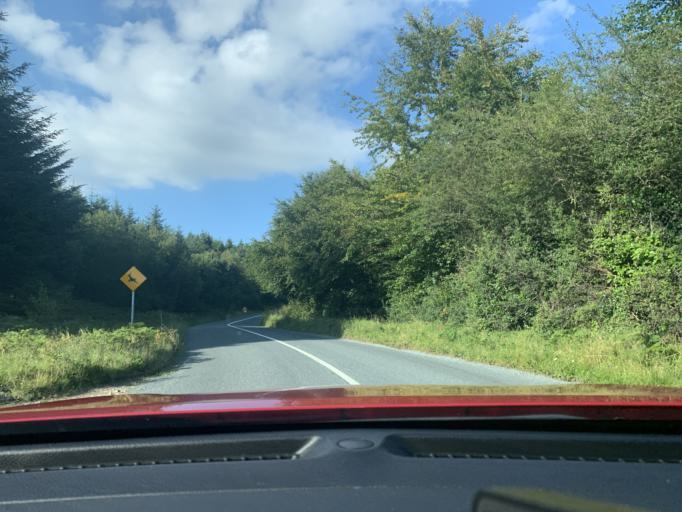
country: IE
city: Ballisodare
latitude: 54.1913
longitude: -8.5826
